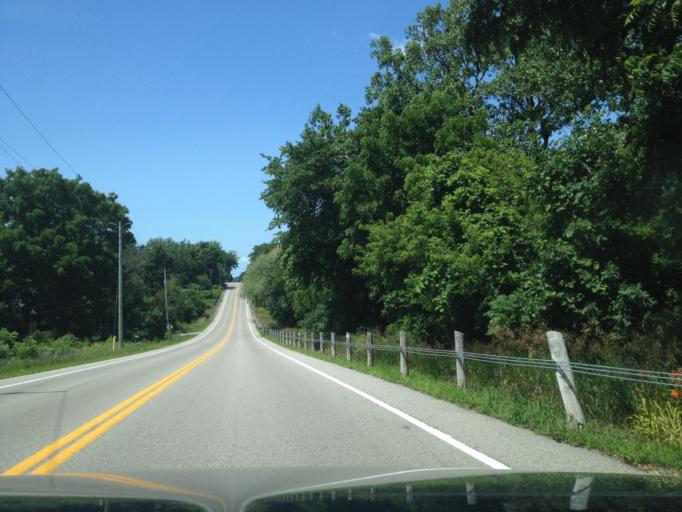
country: CA
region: Ontario
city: Norfolk County
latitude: 42.5816
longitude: -80.5873
